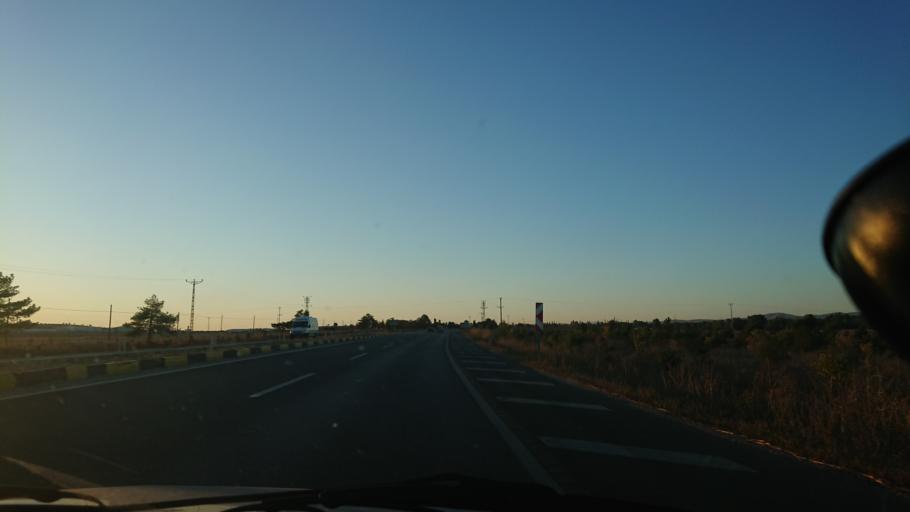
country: TR
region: Eskisehir
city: Mahmudiye
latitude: 39.5568
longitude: 30.9204
